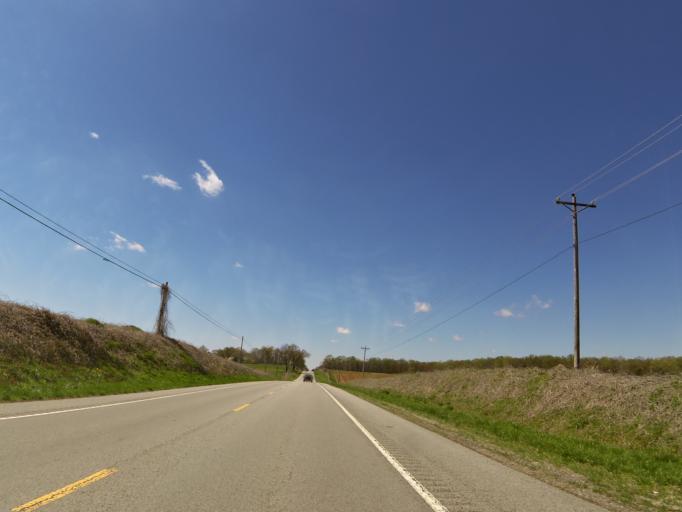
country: US
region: Tennessee
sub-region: White County
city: Sparta
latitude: 35.9509
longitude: -85.5474
